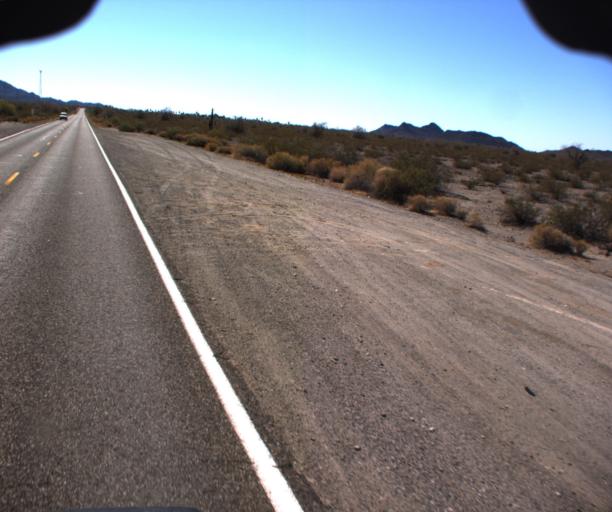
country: US
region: Arizona
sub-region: La Paz County
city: Salome
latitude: 33.7302
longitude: -113.7180
